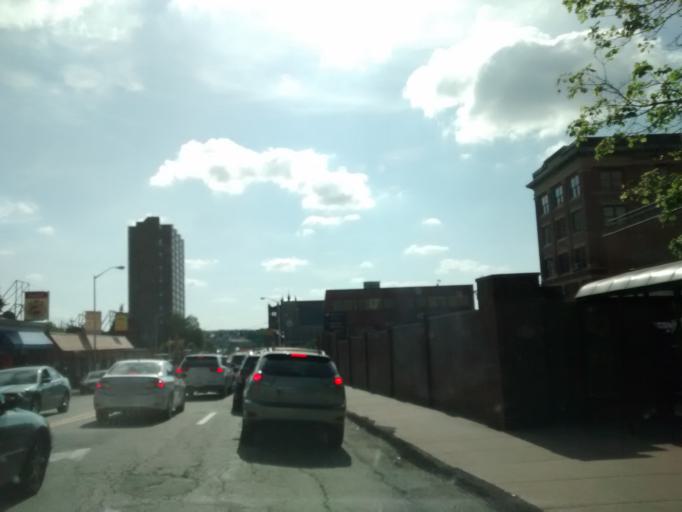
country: US
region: Massachusetts
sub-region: Worcester County
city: Worcester
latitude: 42.2721
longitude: -71.7926
